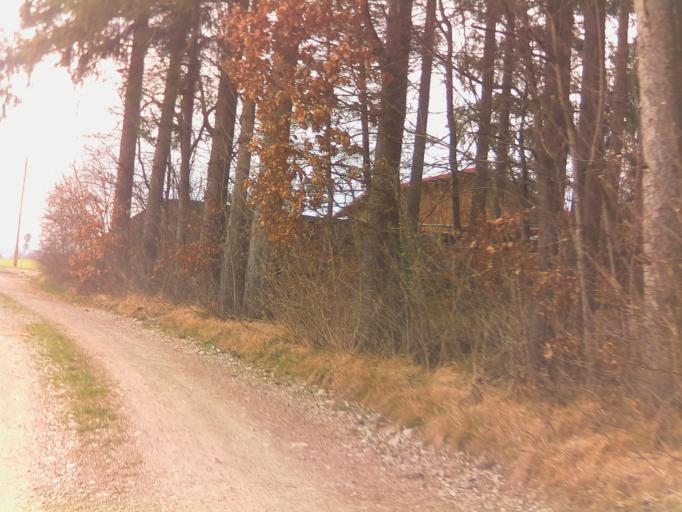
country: DE
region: Bavaria
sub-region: Upper Bavaria
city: Bernried
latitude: 47.8507
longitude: 11.2304
